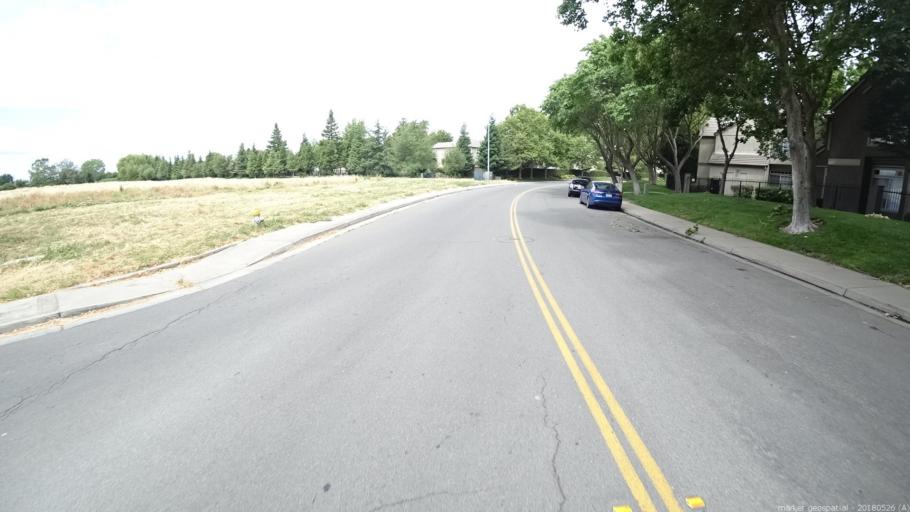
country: US
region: California
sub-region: Yolo County
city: West Sacramento
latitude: 38.6174
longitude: -121.5200
